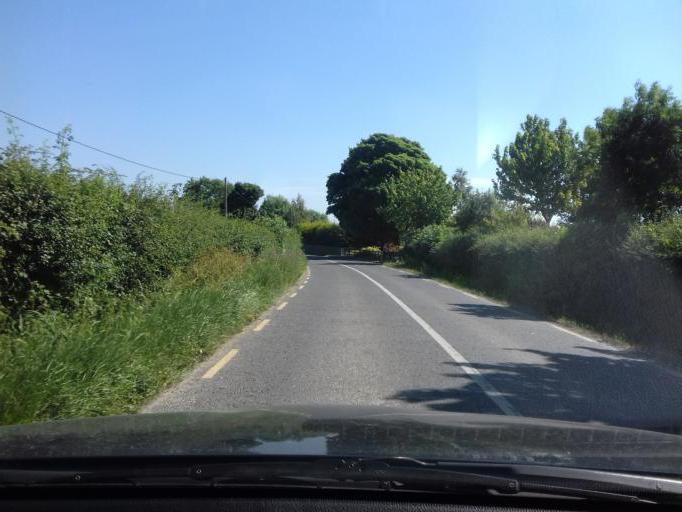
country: IE
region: Leinster
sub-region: Fingal County
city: Swords
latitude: 53.5314
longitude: -6.2702
